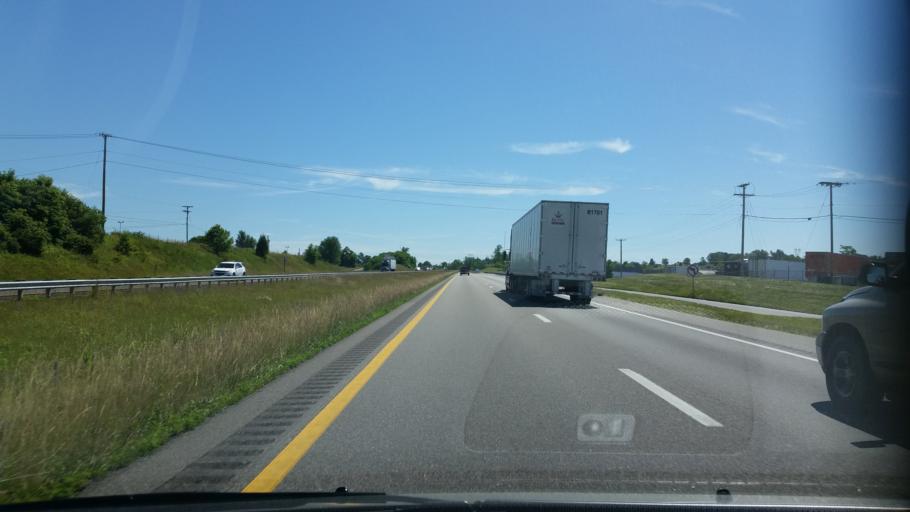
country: US
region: Virginia
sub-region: Washington County
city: Glade Spring
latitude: 36.7722
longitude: -81.7792
